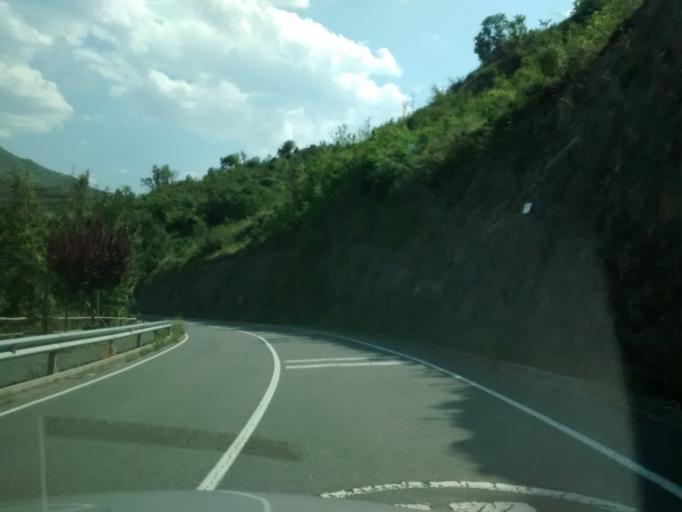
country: ES
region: La Rioja
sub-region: Provincia de La Rioja
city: Soto en Cameros
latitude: 42.2886
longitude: -2.4284
